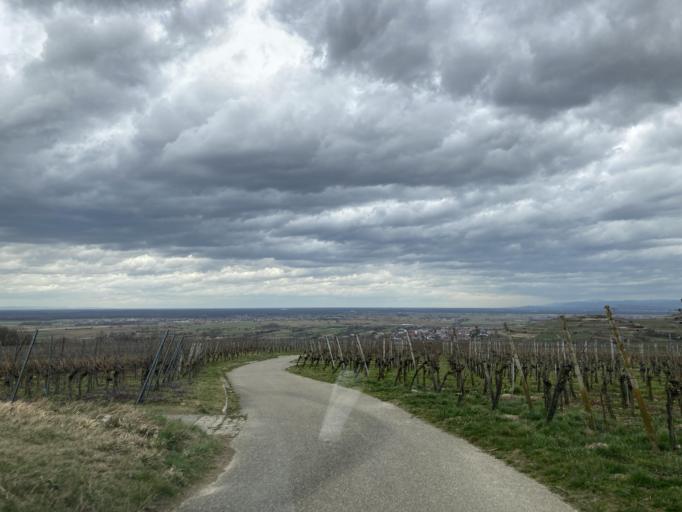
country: DE
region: Baden-Wuerttemberg
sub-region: Freiburg Region
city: Vogtsburg
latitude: 48.1172
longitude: 7.6458
